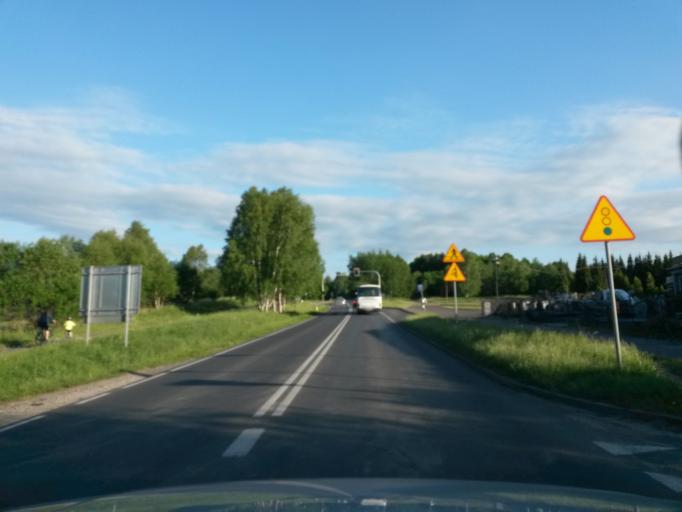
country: PL
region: Lower Silesian Voivodeship
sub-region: Jelenia Gora
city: Jelenia Gora
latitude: 50.8825
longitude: 15.7584
